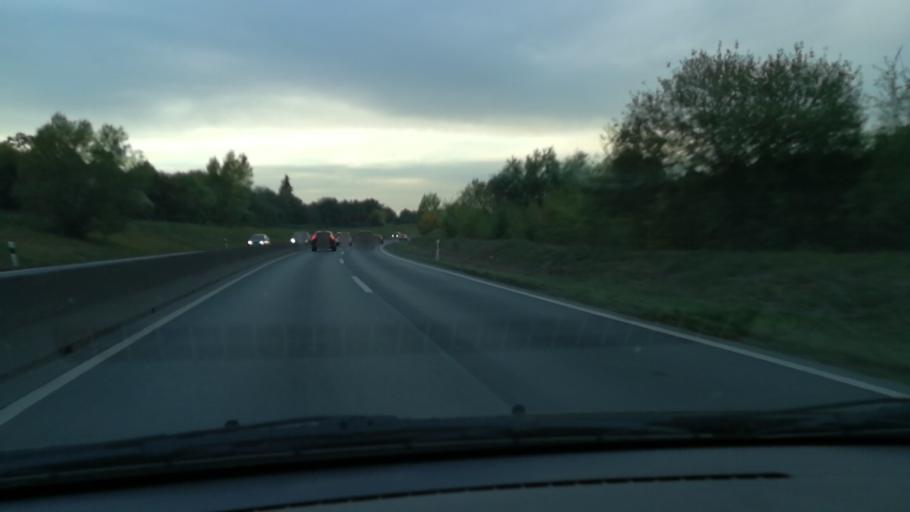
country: DE
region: Hesse
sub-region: Regierungsbezirk Darmstadt
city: Frankfurt am Main
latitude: 50.1392
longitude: 8.7086
